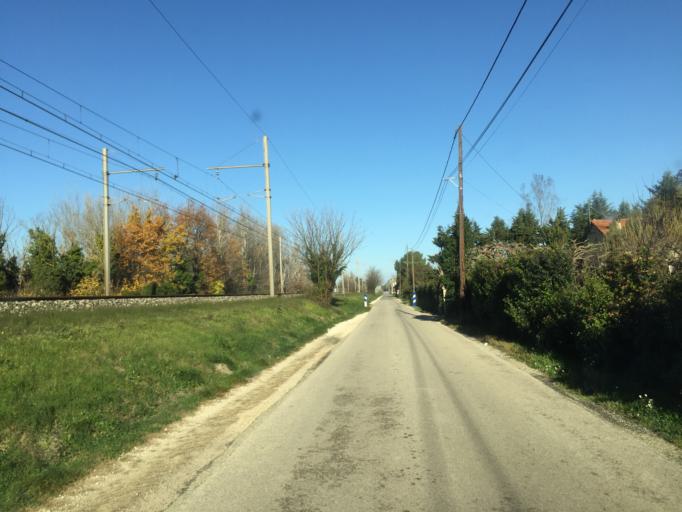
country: FR
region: Provence-Alpes-Cote d'Azur
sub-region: Departement du Vaucluse
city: Courthezon
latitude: 44.0796
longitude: 4.8900
